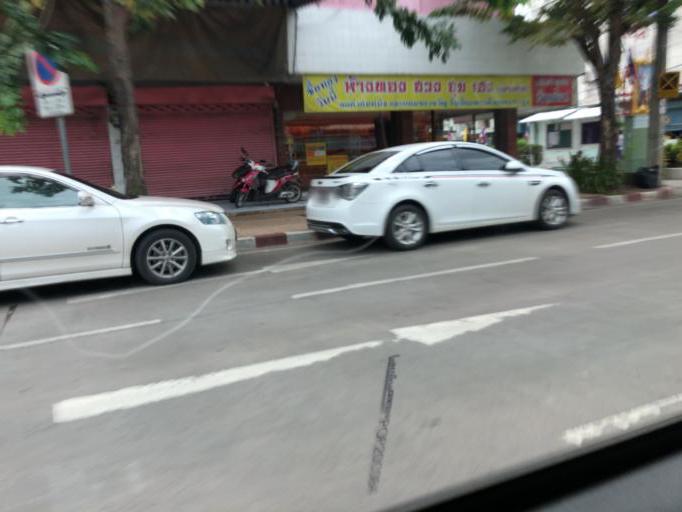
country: TH
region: Bangkok
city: Don Mueang
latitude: 13.9249
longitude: 100.5949
